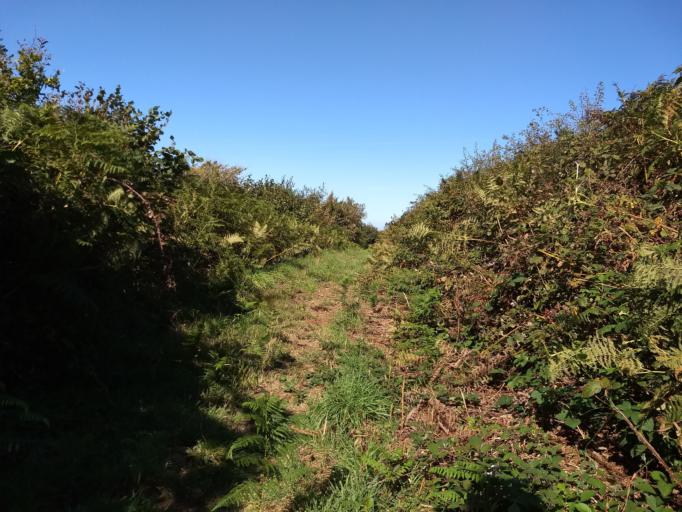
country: GB
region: England
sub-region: Isle of Wight
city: Niton
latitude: 50.6309
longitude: -1.2790
